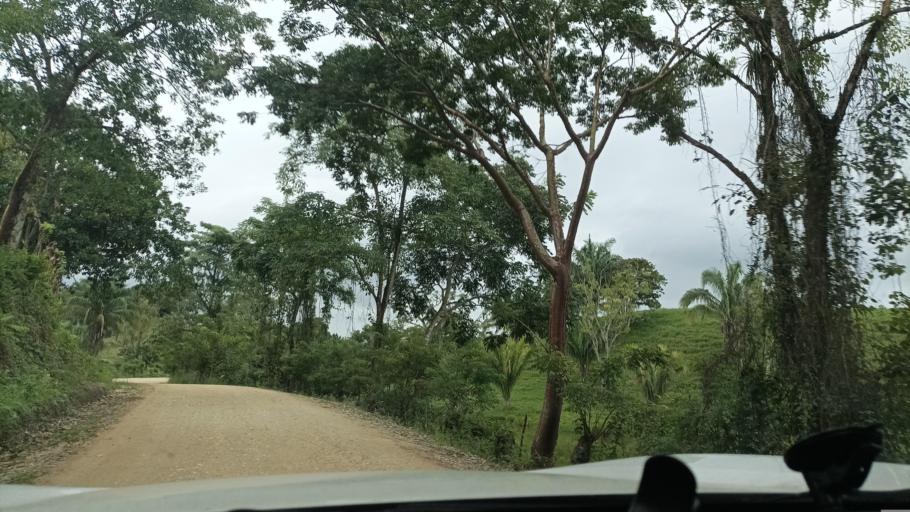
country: MX
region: Veracruz
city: Hidalgotitlan
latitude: 17.6487
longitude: -94.5017
